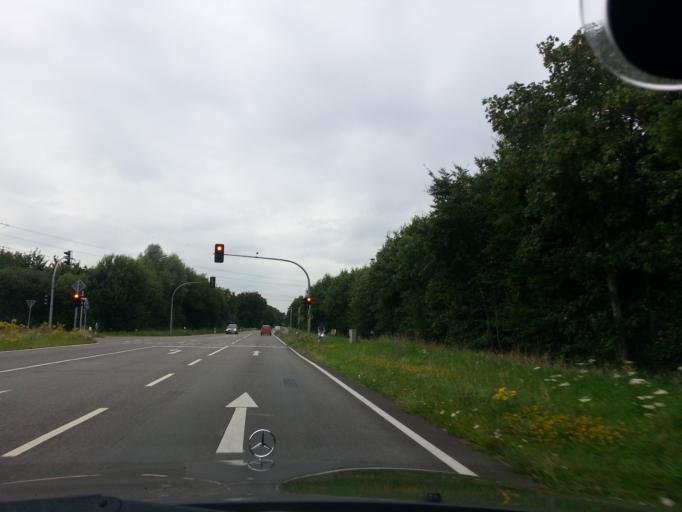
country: DE
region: North Rhine-Westphalia
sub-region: Regierungsbezirk Munster
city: Raesfeld
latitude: 51.7849
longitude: 6.8441
